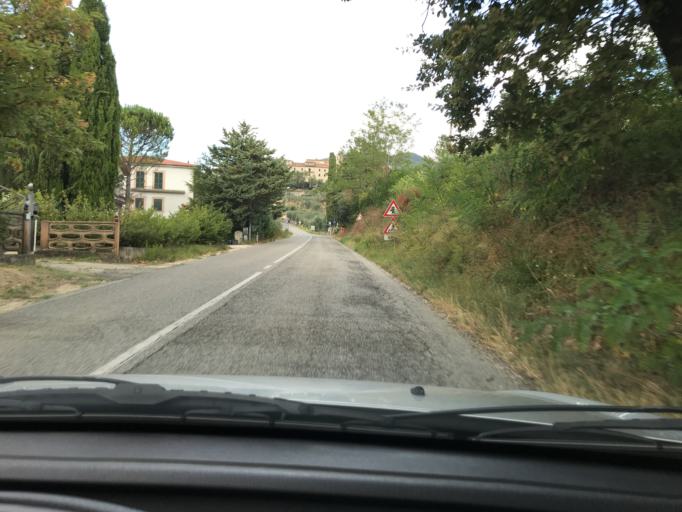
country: IT
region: Umbria
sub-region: Provincia di Terni
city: Montecchio
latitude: 42.6600
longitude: 12.2814
